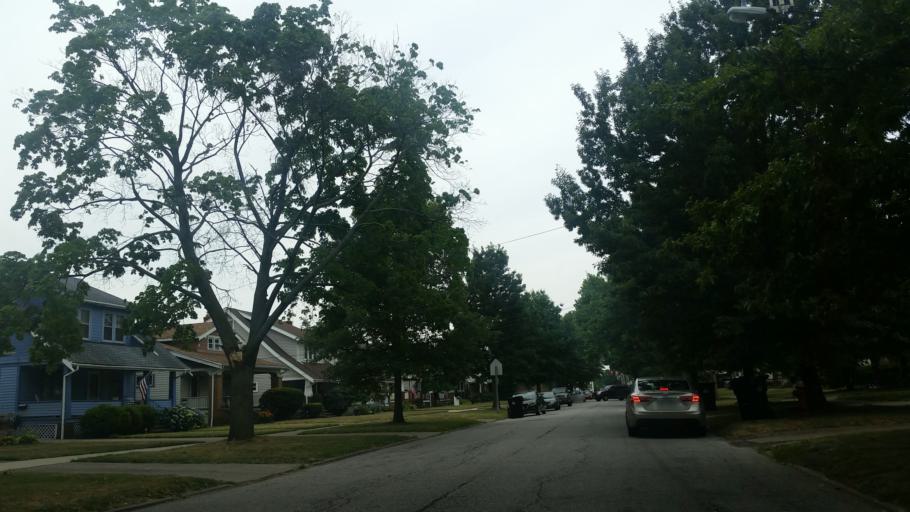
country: US
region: Ohio
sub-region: Cuyahoga County
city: Brooklyn Heights
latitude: 41.4266
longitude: -81.7069
